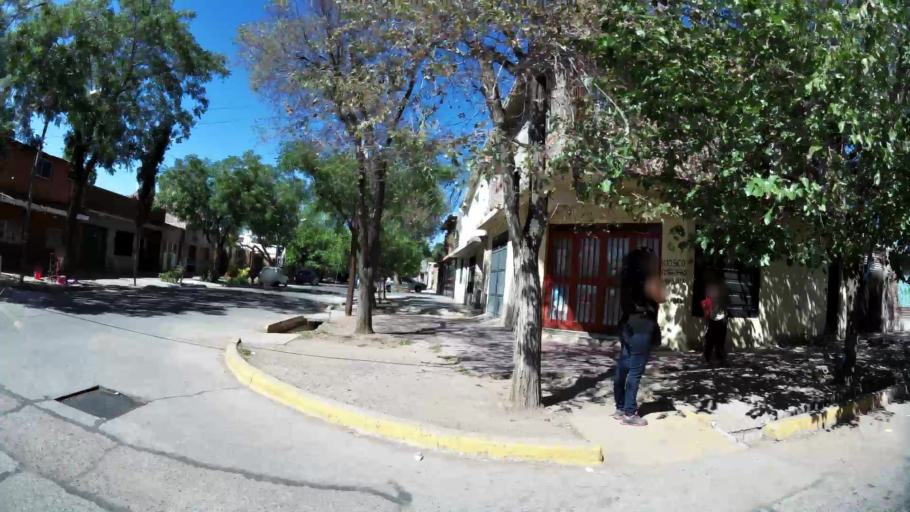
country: AR
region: Mendoza
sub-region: Departamento de Godoy Cruz
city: Godoy Cruz
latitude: -32.9048
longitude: -68.8647
